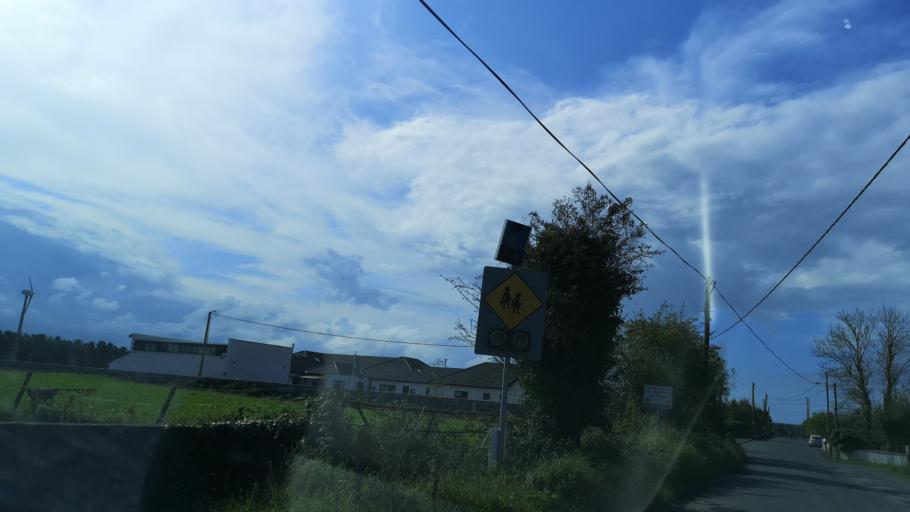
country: IE
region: Connaught
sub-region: County Galway
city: Oranmore
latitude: 53.2928
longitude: -8.8433
